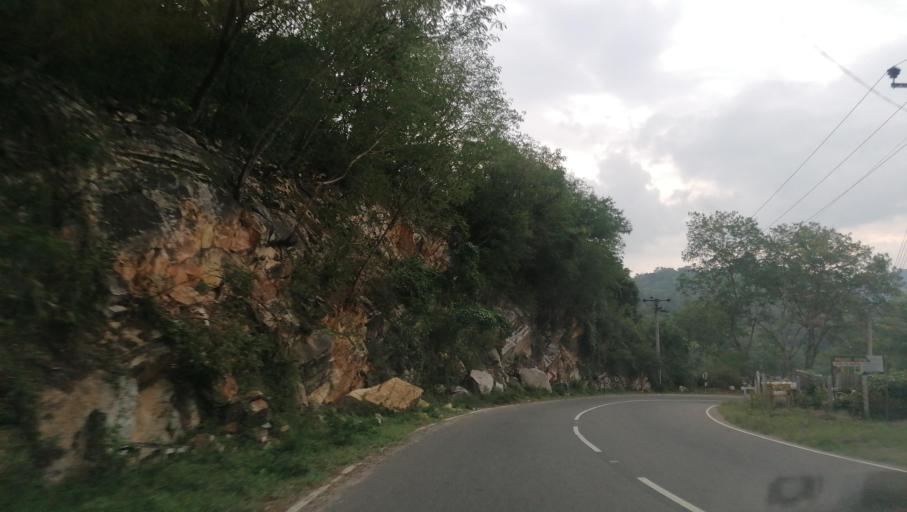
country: LK
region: Central
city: Kandy
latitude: 7.2224
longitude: 80.7627
